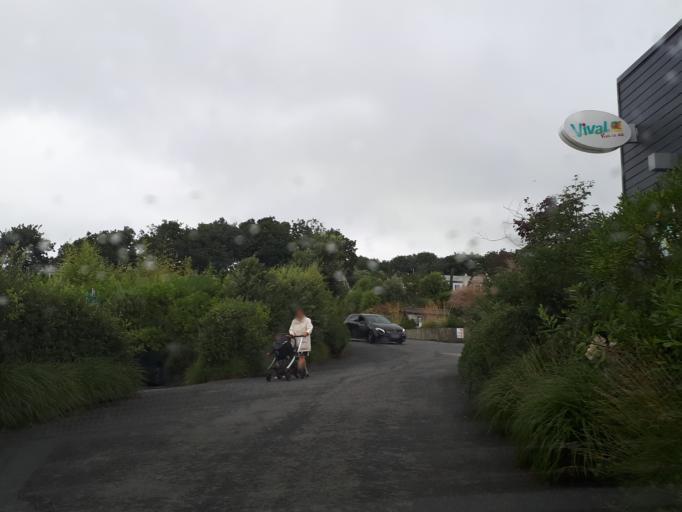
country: FR
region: Brittany
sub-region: Departement du Finistere
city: Carantec
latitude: 48.6577
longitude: -3.9288
